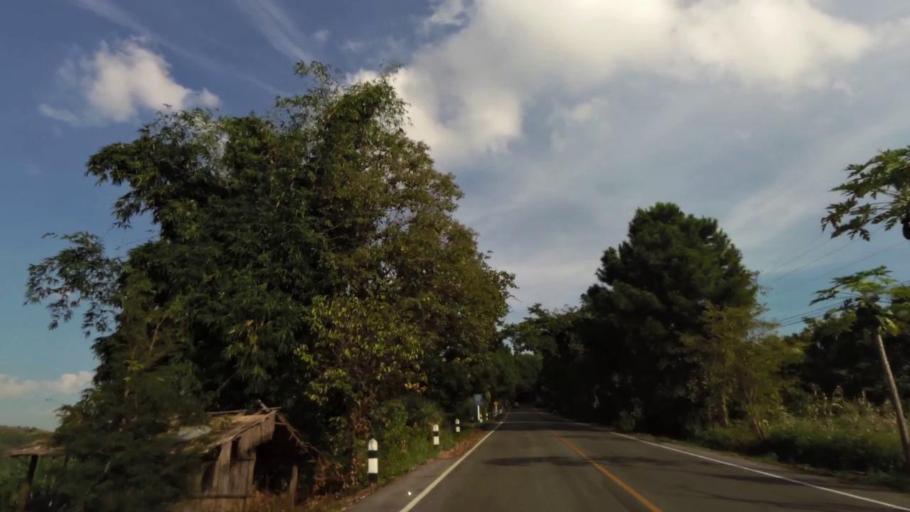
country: TH
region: Chiang Rai
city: Khun Tan
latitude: 19.8710
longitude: 100.3242
